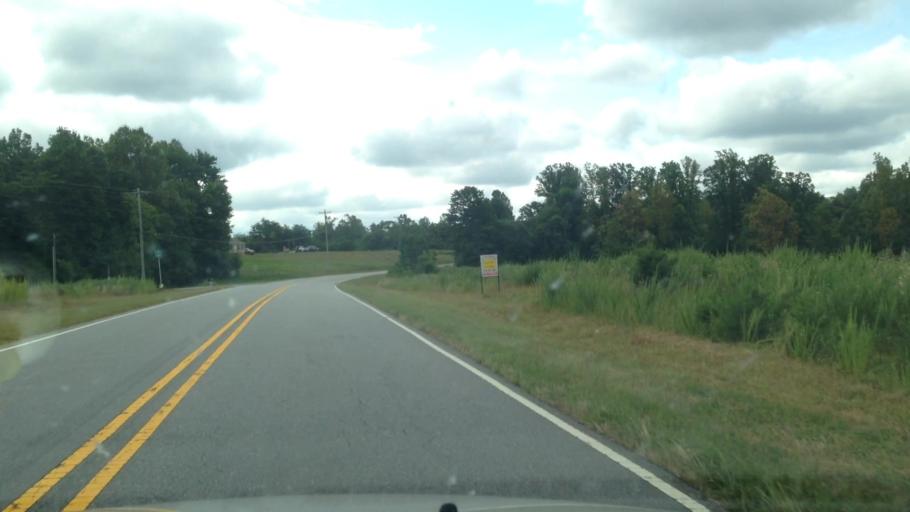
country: US
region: North Carolina
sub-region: Rockingham County
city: Mayodan
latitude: 36.4201
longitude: -80.0705
